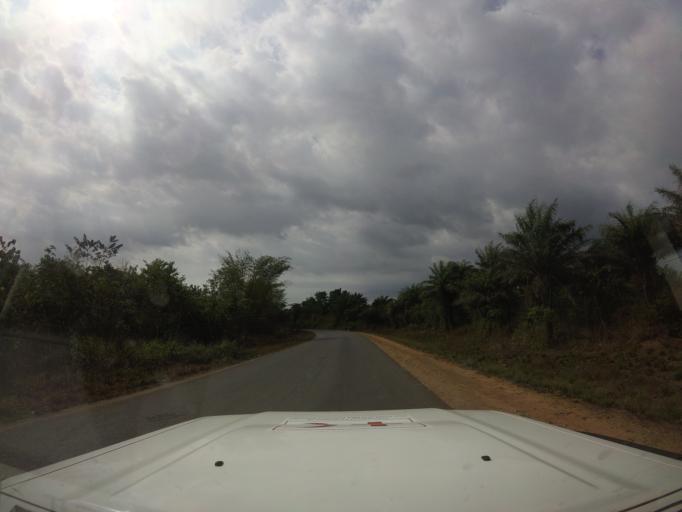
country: LR
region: Montserrado
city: Monrovia
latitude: 6.4986
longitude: -10.8122
